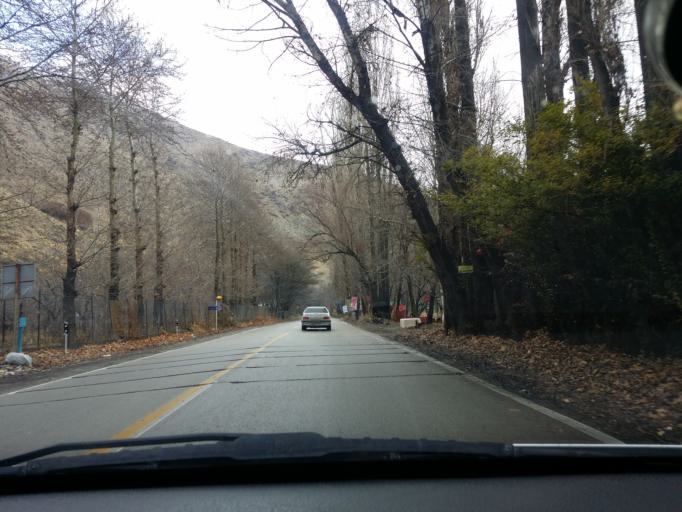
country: IR
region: Tehran
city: Tajrish
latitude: 36.0248
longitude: 51.2500
